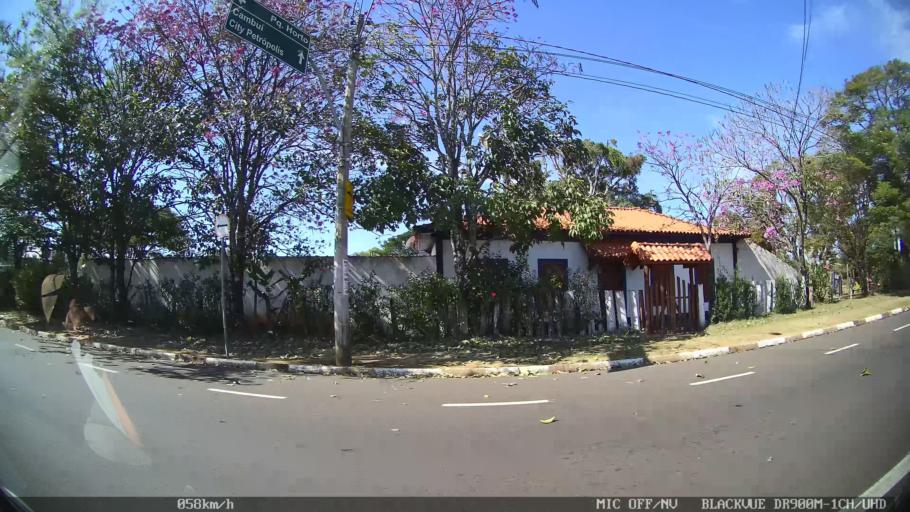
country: BR
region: Sao Paulo
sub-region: Franca
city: Franca
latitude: -20.4949
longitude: -47.3982
